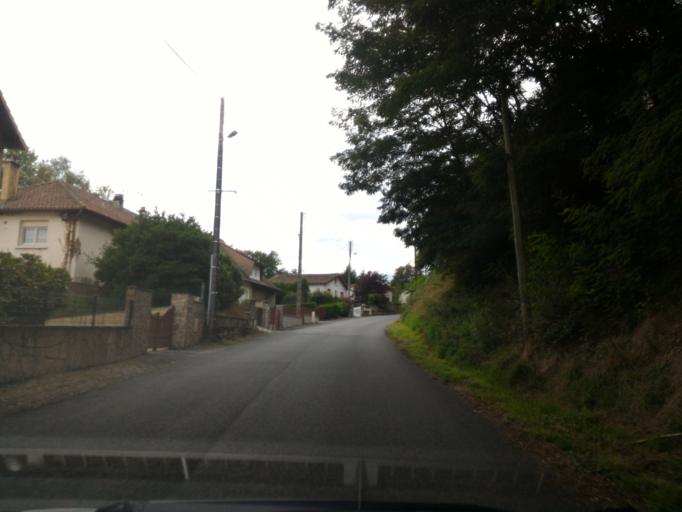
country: FR
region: Limousin
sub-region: Departement de la Haute-Vienne
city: Saint-Junien
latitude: 45.8930
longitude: 0.8848
